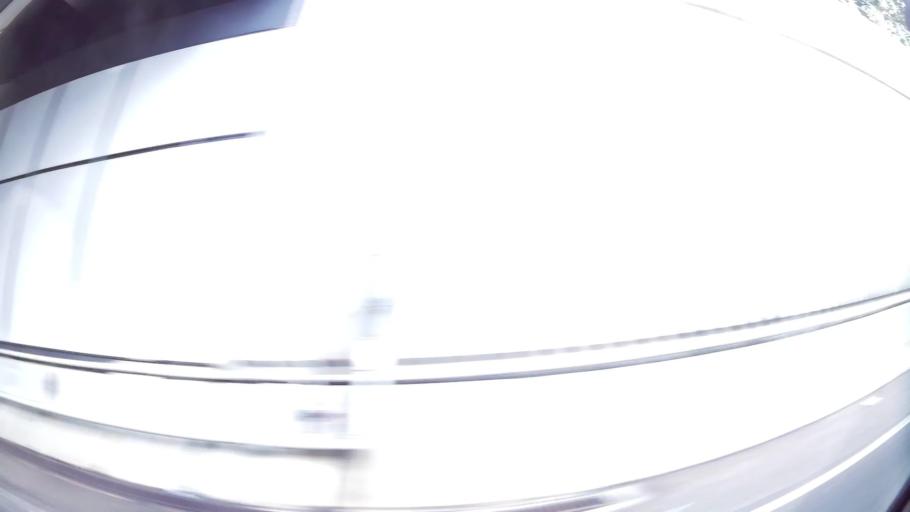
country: HK
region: Kowloon City
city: Kowloon
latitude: 22.2894
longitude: 114.2149
